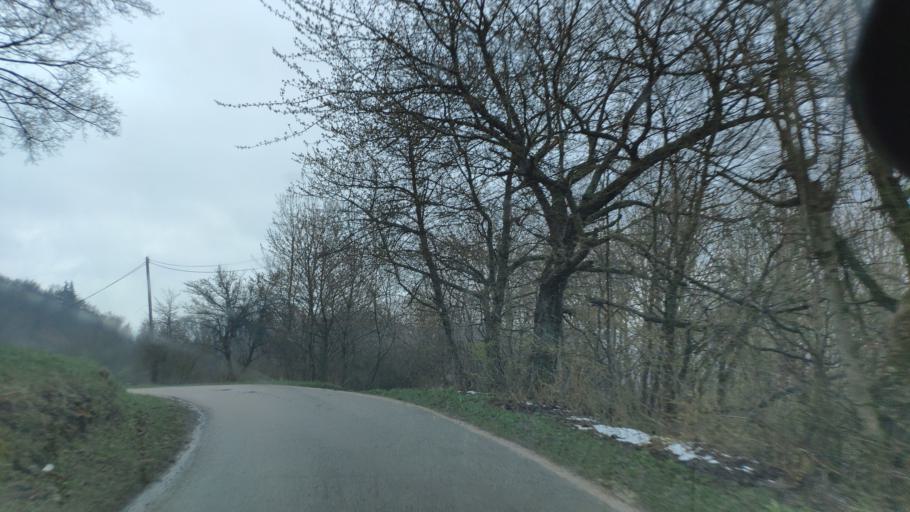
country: SK
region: Nitriansky
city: Stara Tura
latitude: 48.8251
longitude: 17.7017
